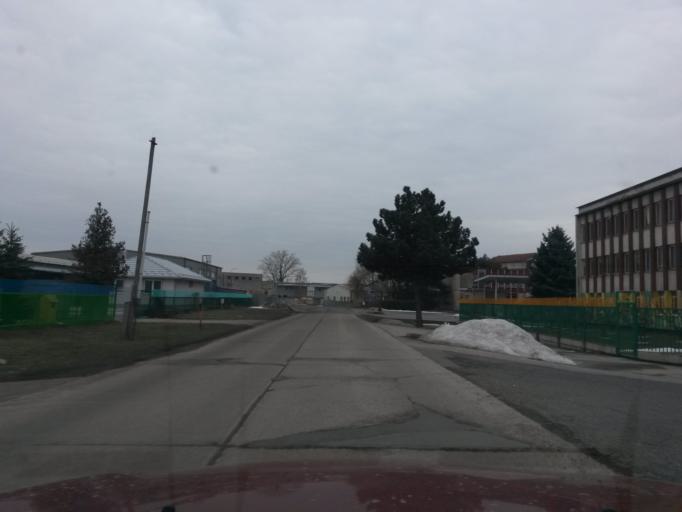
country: SK
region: Kosicky
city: Michalovce
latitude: 48.7475
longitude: 21.8890
